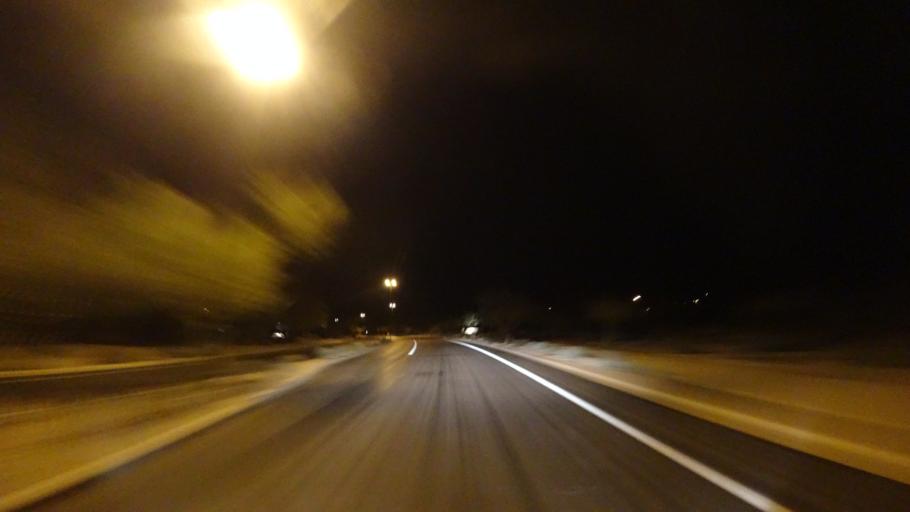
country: US
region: Arizona
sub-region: Pinal County
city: Apache Junction
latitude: 33.4814
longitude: -111.6589
